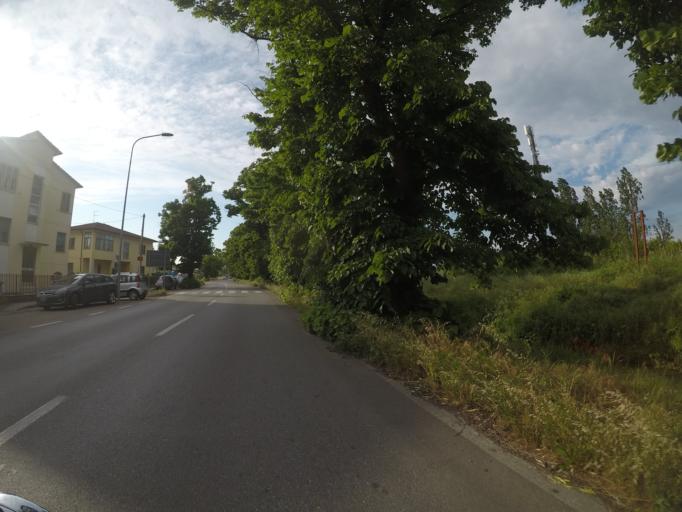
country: IT
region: Tuscany
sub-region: Province of Pisa
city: Madonna dell'Acqua
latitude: 43.7296
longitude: 10.3882
